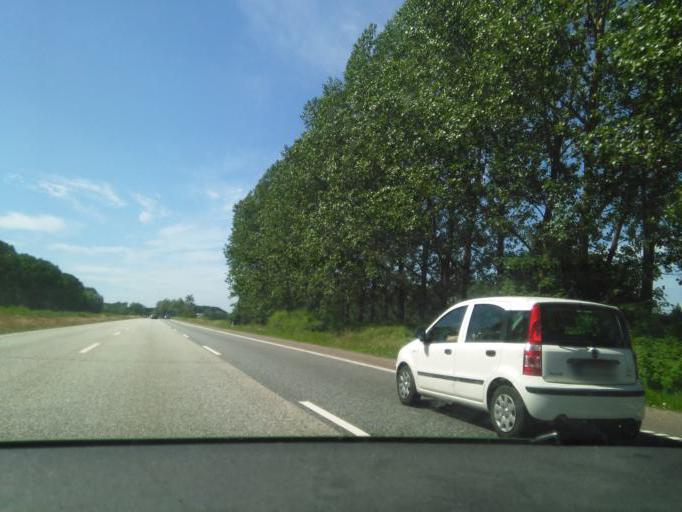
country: DK
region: Capital Region
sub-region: Hoje-Taastrup Kommune
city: Taastrup
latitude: 55.6648
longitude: 12.2699
